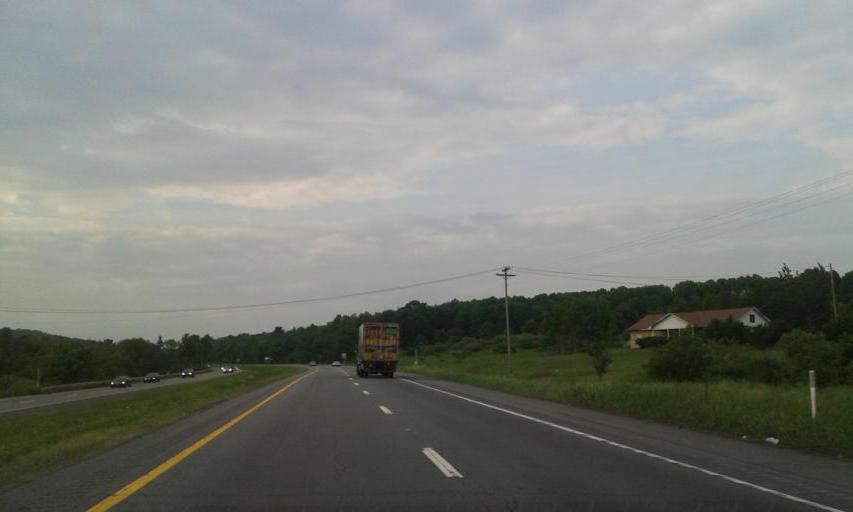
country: US
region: Pennsylvania
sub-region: Susquehanna County
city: Susquehanna
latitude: 41.8241
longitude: -75.6803
